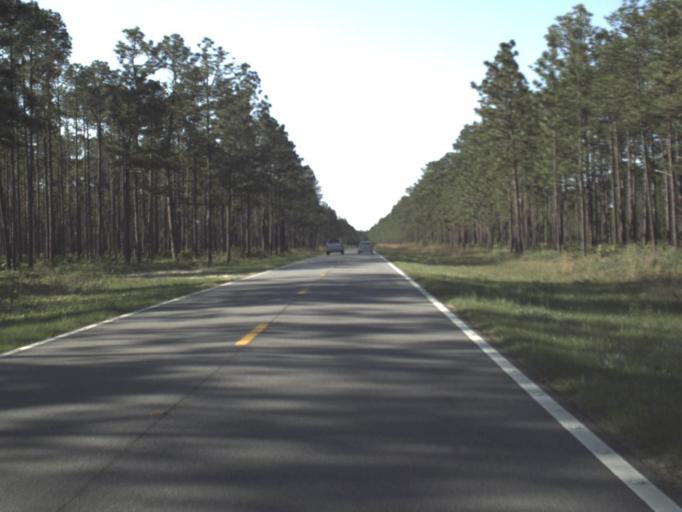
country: US
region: Florida
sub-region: Gulf County
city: Wewahitchka
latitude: 30.1160
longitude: -84.9877
